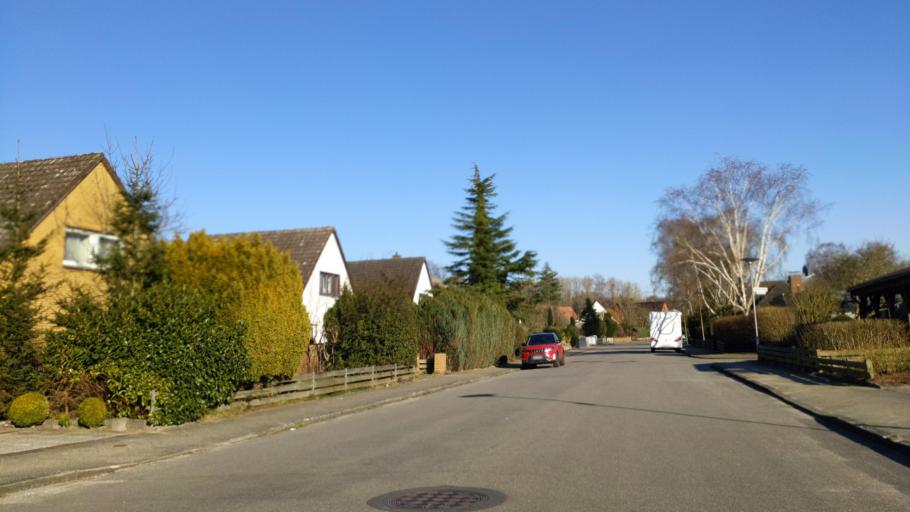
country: DE
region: Schleswig-Holstein
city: Luebeck
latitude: 53.8761
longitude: 10.7263
